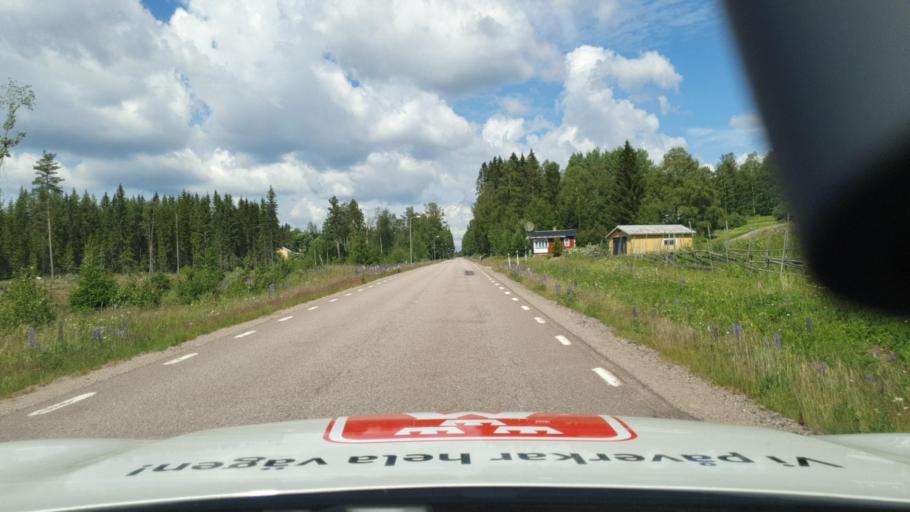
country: SE
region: Vaermland
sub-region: Torsby Kommun
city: Torsby
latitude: 60.4611
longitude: 12.8847
